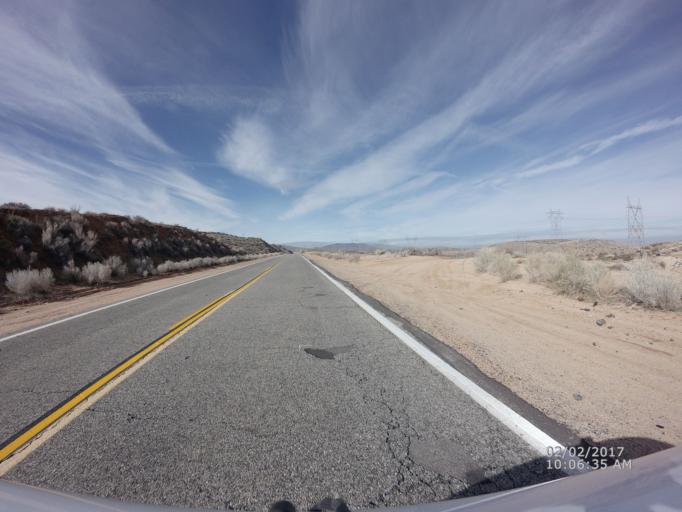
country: US
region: California
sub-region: Los Angeles County
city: Littlerock
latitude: 34.5066
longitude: -118.0008
